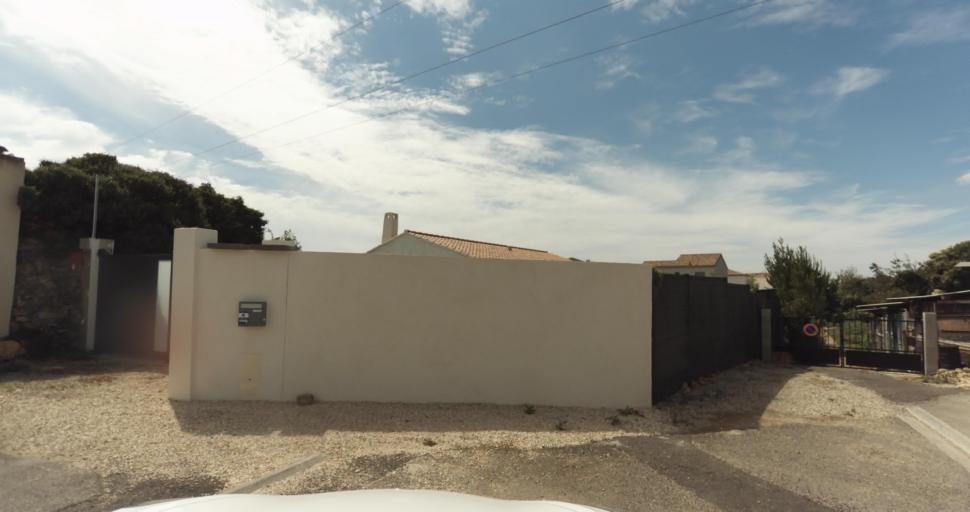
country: FR
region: Provence-Alpes-Cote d'Azur
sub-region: Departement des Bouches-du-Rhone
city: Miramas
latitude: 43.5883
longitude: 5.0182
